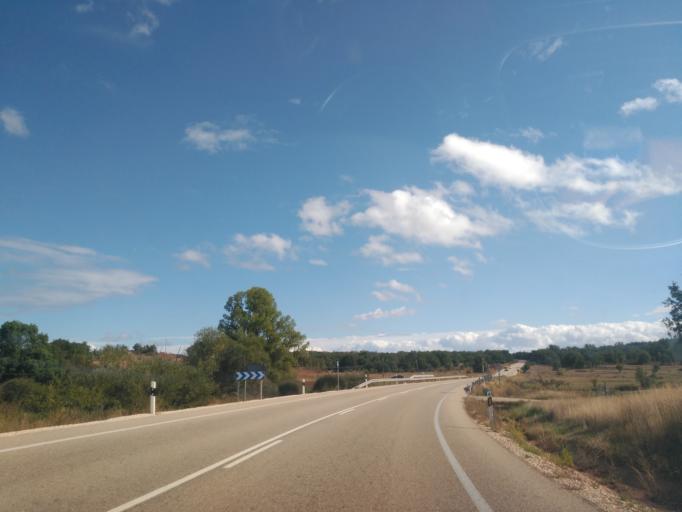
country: ES
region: Castille and Leon
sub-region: Provincia de Burgos
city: Pinilla de los Barruecos
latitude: 41.9373
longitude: -3.2853
